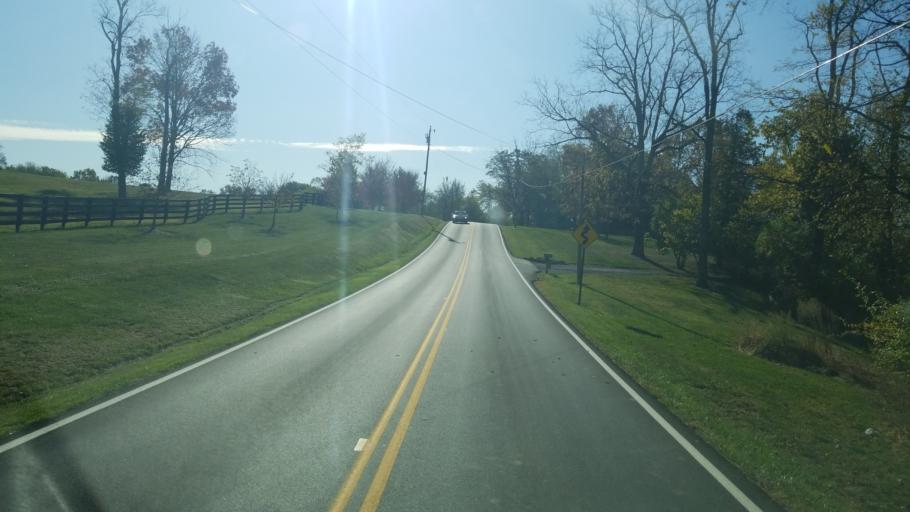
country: US
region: Ohio
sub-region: Warren County
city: Morrow
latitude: 39.3893
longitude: -84.0700
